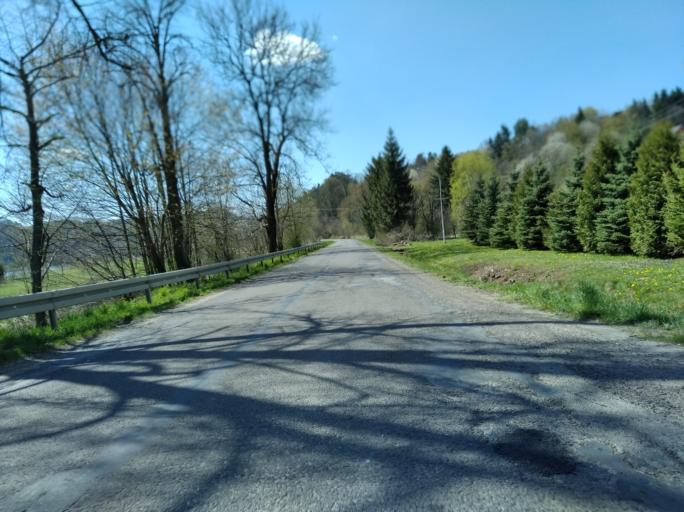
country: PL
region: Subcarpathian Voivodeship
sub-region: Powiat brzozowski
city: Dydnia
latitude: 49.7042
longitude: 22.1959
